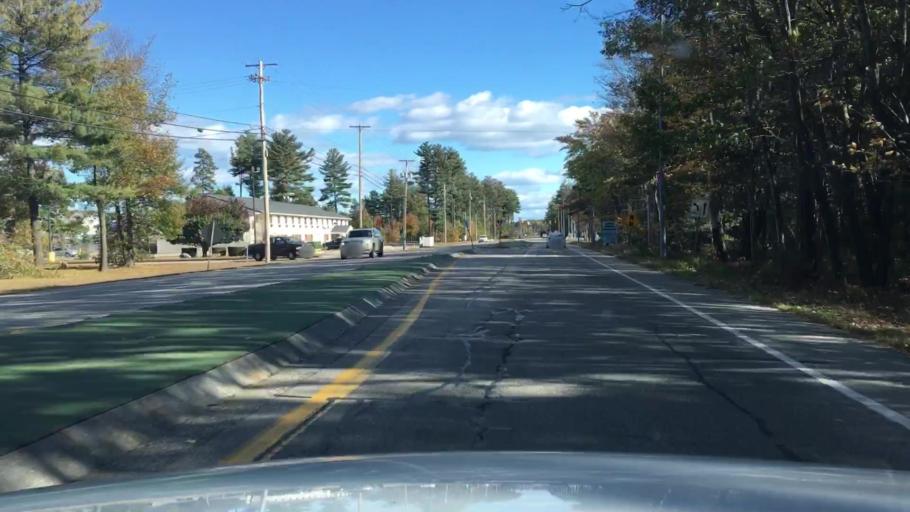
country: US
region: Maine
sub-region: York County
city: South Sanford
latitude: 43.4009
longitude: -70.7059
